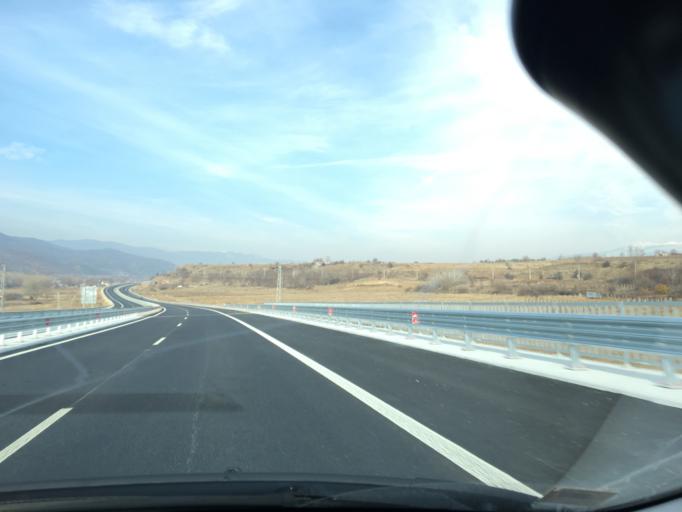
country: BG
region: Blagoevgrad
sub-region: Obshtina Sandanski
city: Sandanski
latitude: 41.5529
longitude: 23.2498
